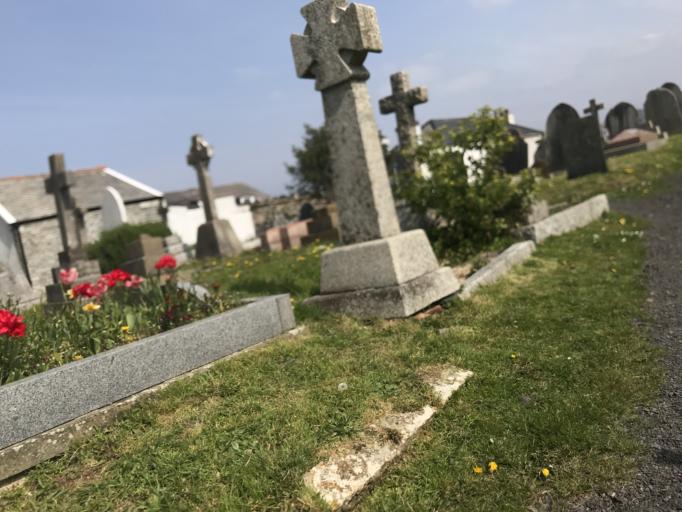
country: GB
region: England
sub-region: Devon
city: Ilfracombe
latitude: 51.2059
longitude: -4.1290
